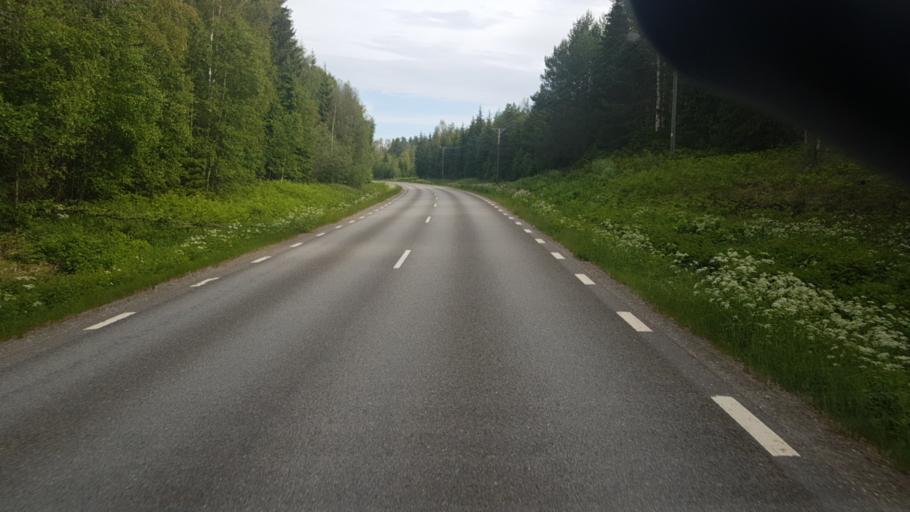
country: SE
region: Vaermland
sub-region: Arvika Kommun
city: Arvika
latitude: 59.7212
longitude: 12.5681
